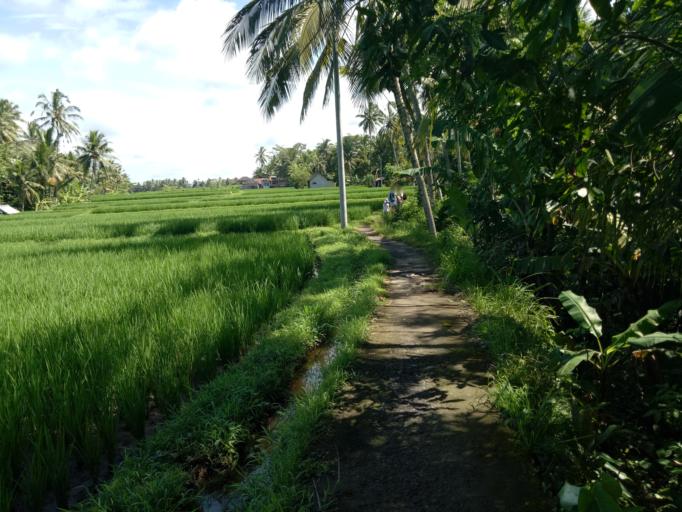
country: ID
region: Bali
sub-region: Kabupaten Gianyar
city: Ubud
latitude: -8.4870
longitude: 115.2617
